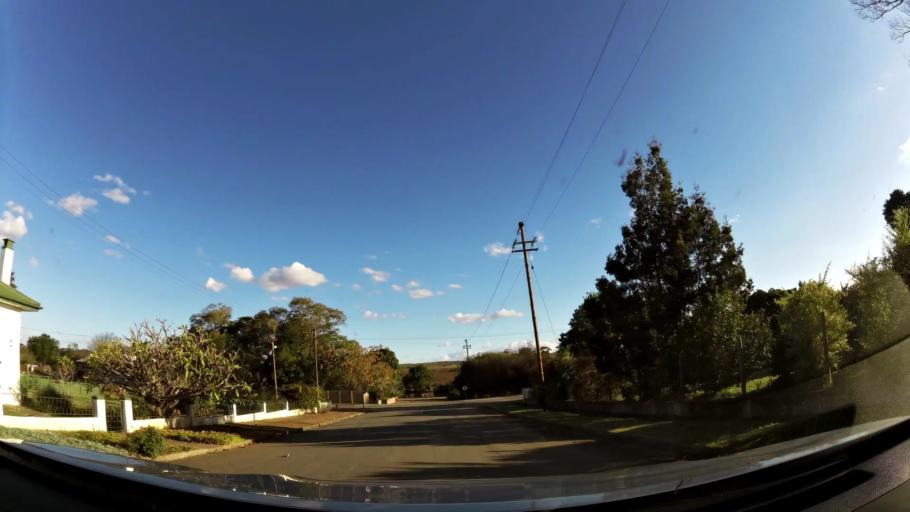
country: ZA
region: Western Cape
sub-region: Eden District Municipality
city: Riversdale
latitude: -34.0843
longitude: 20.9485
